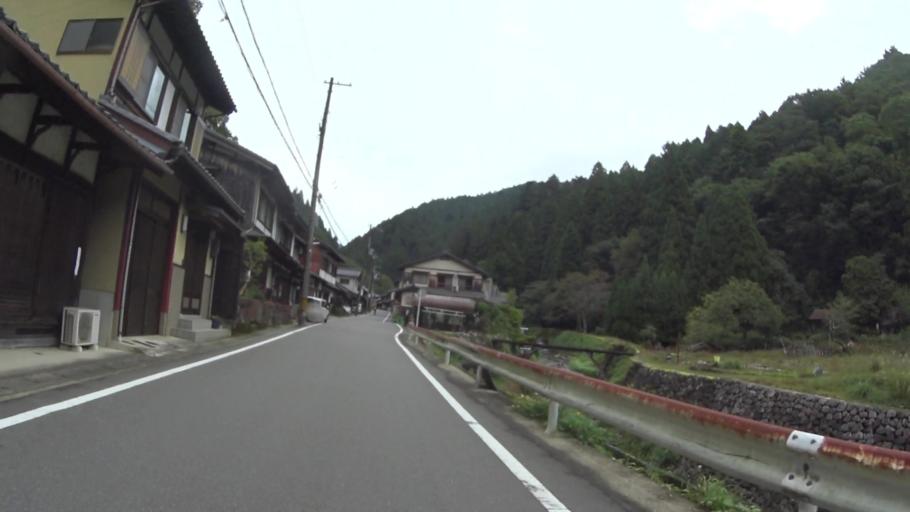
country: JP
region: Kyoto
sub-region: Kyoto-shi
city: Kamigyo-ku
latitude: 35.1159
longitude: 135.7746
